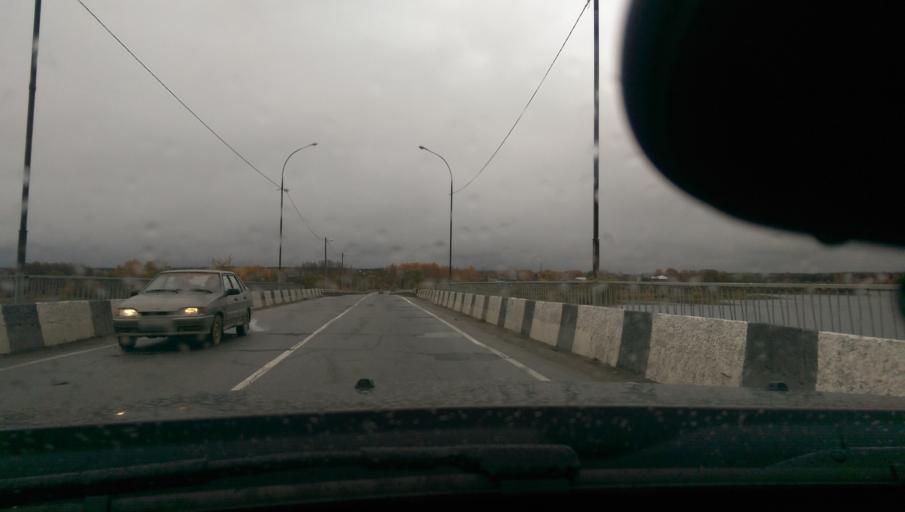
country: RU
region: Jaroslavl
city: Poshekhon'ye
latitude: 58.5105
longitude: 39.1220
